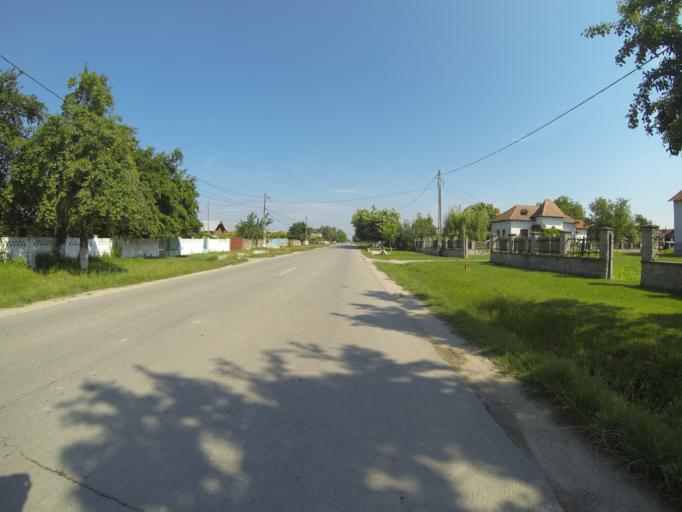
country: RO
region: Gorj
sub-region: Comuna Crusetu
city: Crusetu
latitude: 44.6039
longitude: 23.6902
